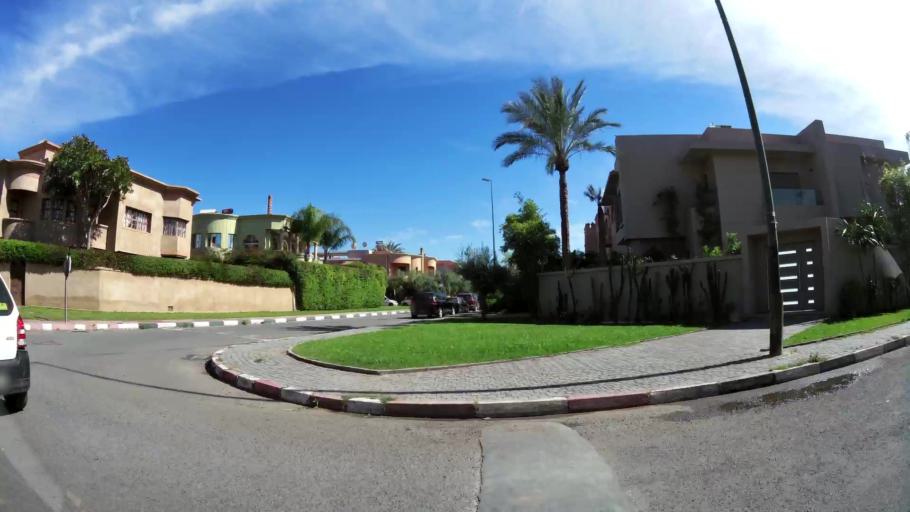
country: MA
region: Marrakech-Tensift-Al Haouz
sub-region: Marrakech
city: Marrakesh
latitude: 31.6519
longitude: -8.0563
